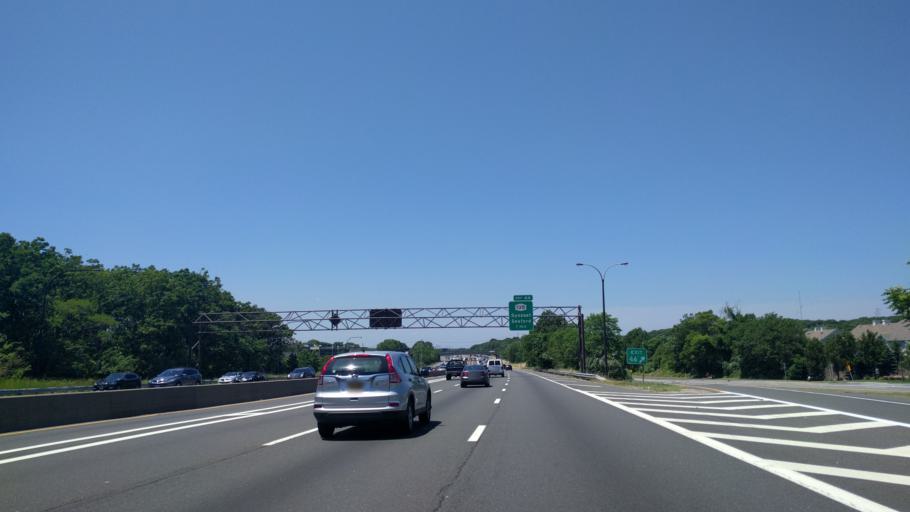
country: US
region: New York
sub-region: Nassau County
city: Plainview
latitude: 40.7931
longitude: -73.4623
